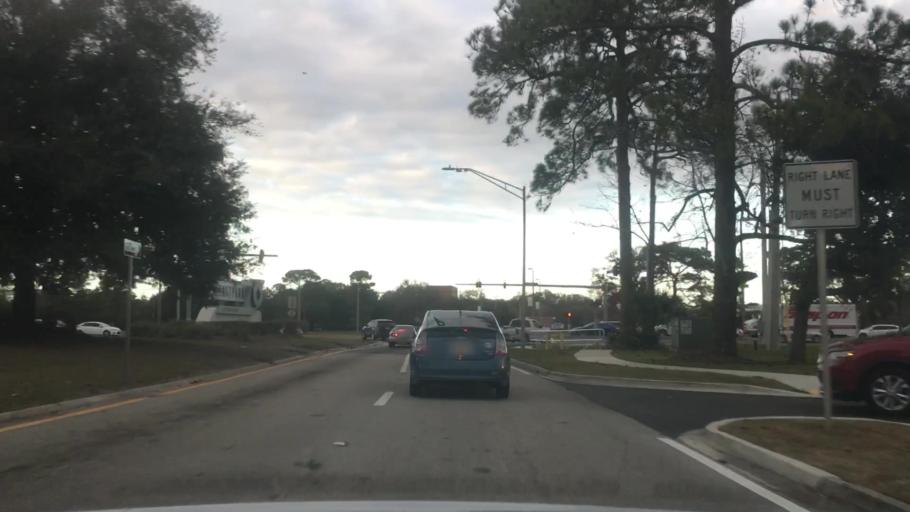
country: US
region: Florida
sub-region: Duval County
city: Neptune Beach
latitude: 30.2864
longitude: -81.5103
